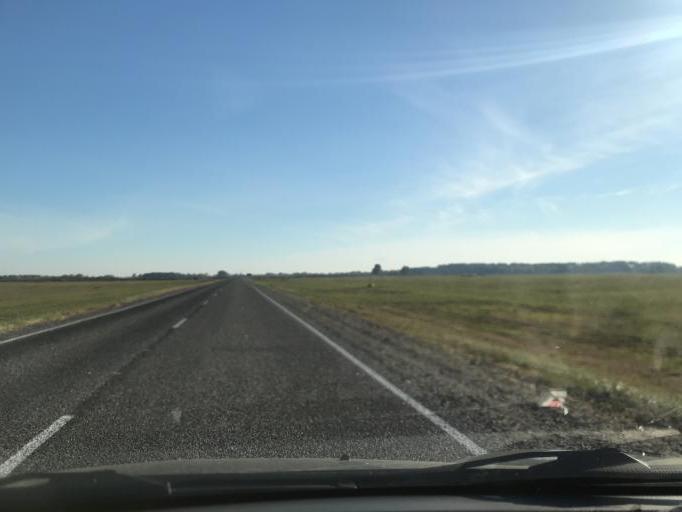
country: BY
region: Gomel
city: Brahin
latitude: 51.7735
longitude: 30.2808
